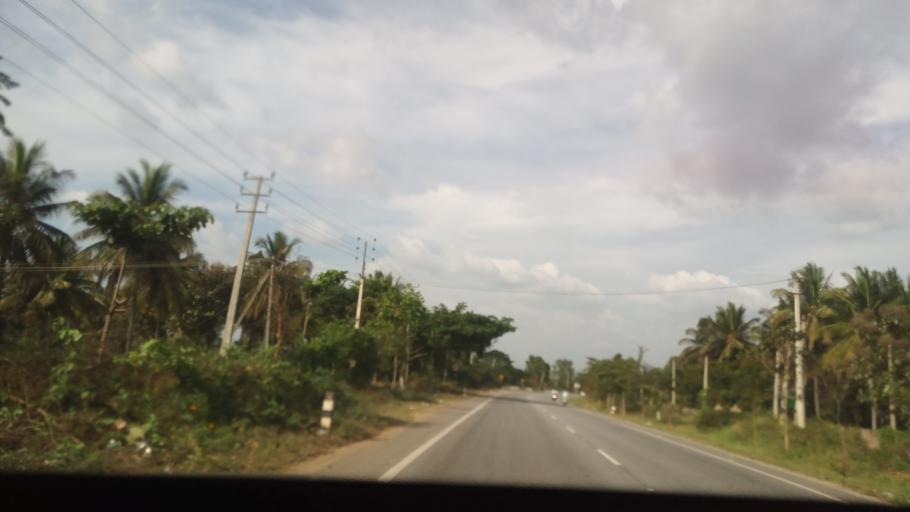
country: IN
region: Karnataka
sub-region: Mandya
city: Maddur
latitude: 12.6715
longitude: 77.0555
